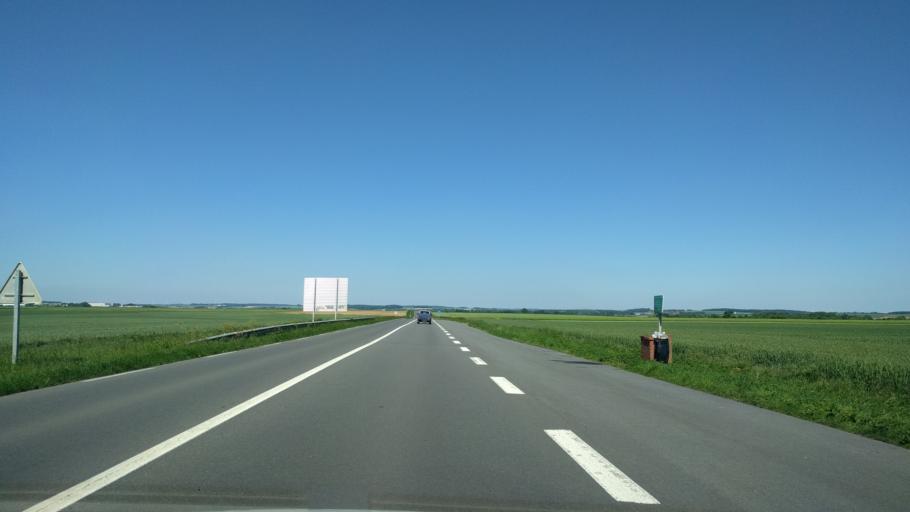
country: FR
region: Picardie
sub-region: Departement de la Somme
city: Peronne
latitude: 49.8796
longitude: 2.8976
